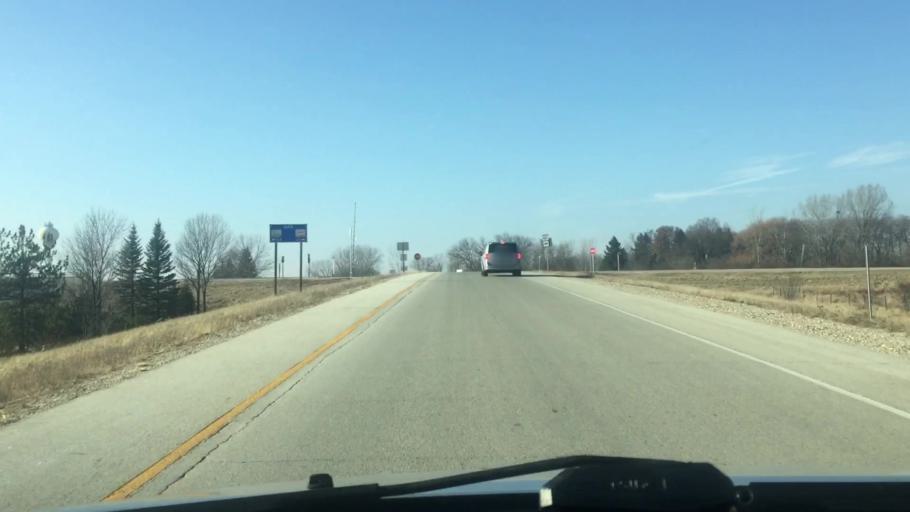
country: US
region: Wisconsin
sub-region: Waukesha County
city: Pewaukee
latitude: 43.0951
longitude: -88.2704
